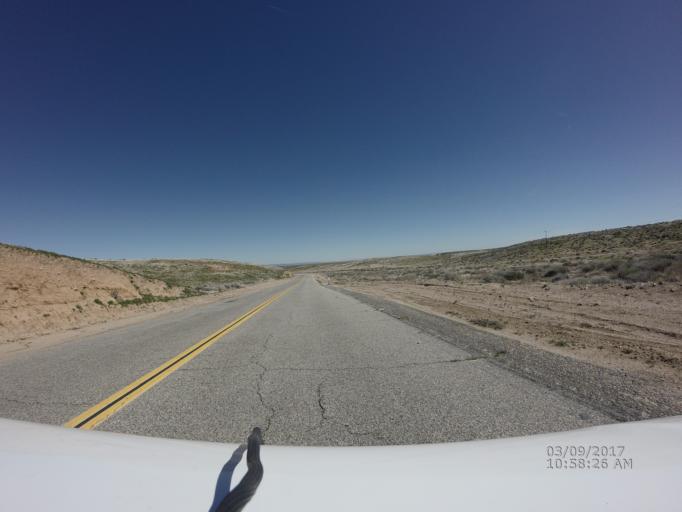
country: US
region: California
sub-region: Los Angeles County
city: Green Valley
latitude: 34.6953
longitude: -118.3821
